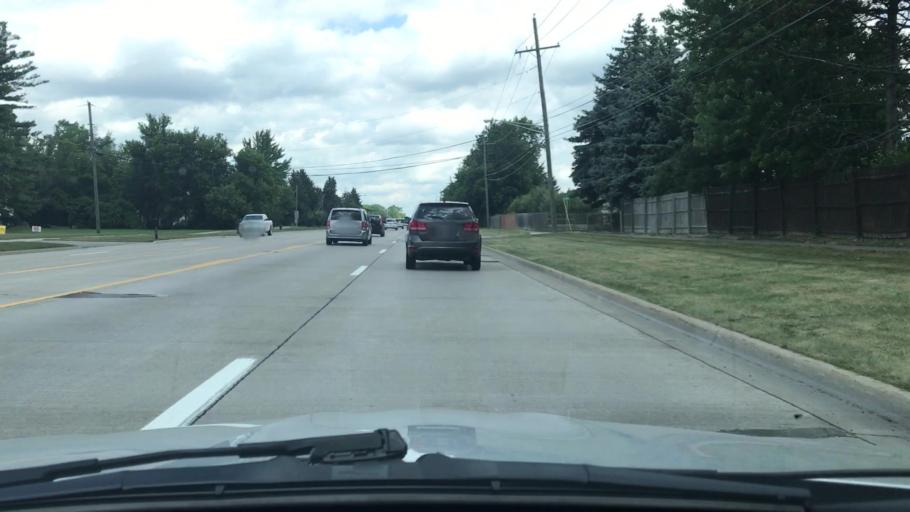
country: US
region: Michigan
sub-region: Macomb County
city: Sterling Heights
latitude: 42.5720
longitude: -83.0890
